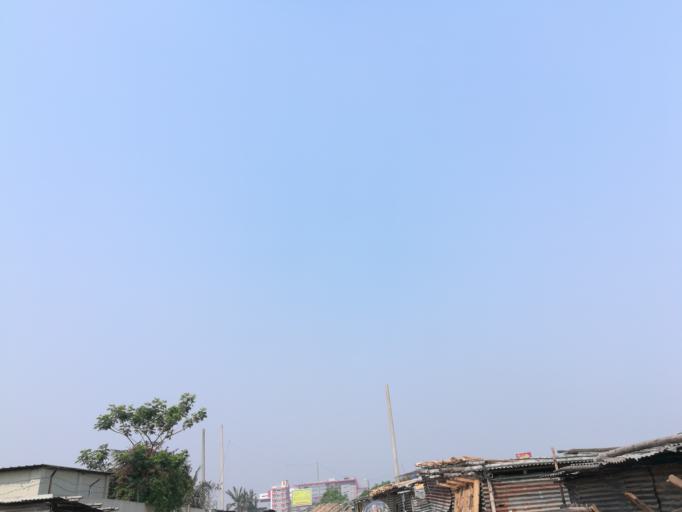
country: BD
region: Dhaka
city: Tungi
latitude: 23.8691
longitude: 90.3774
